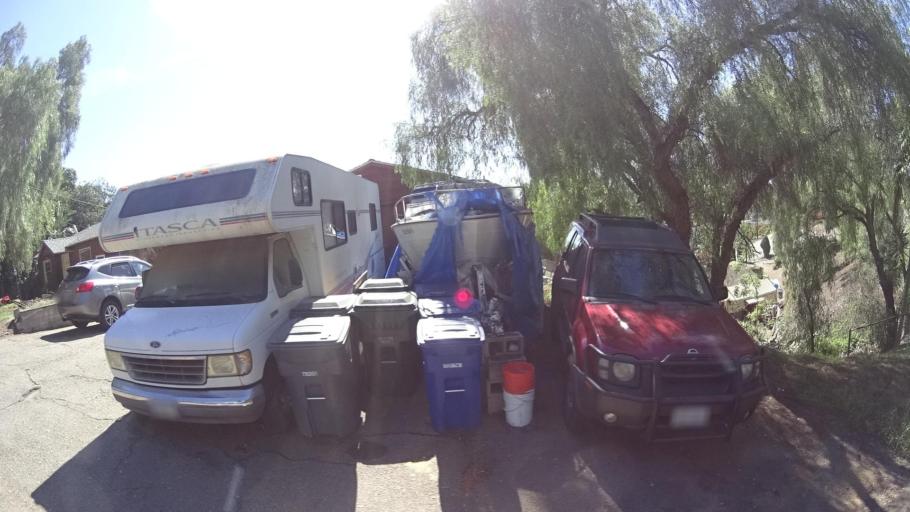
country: US
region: California
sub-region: San Diego County
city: Casa de Oro-Mount Helix
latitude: 32.7460
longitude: -116.9677
